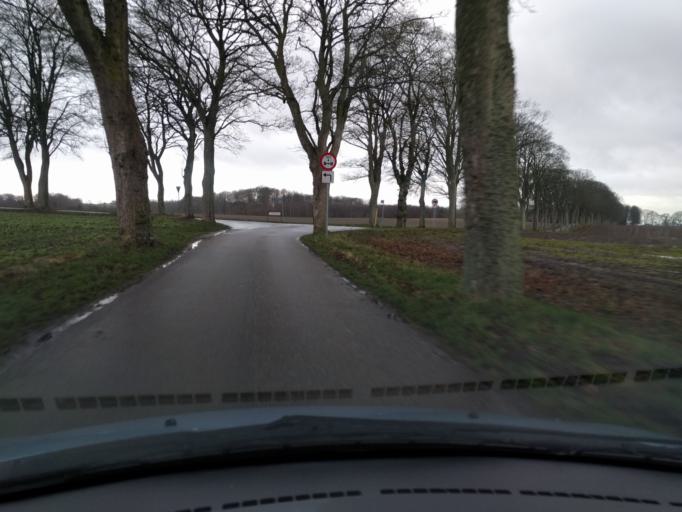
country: DK
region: South Denmark
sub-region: Kerteminde Kommune
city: Langeskov
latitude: 55.3535
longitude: 10.5436
